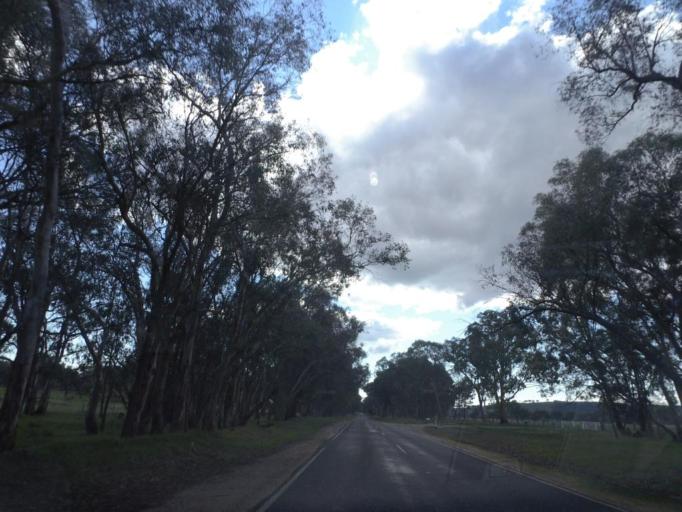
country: AU
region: New South Wales
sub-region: Corowa Shire
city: Howlong
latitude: -36.2046
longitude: 146.6214
